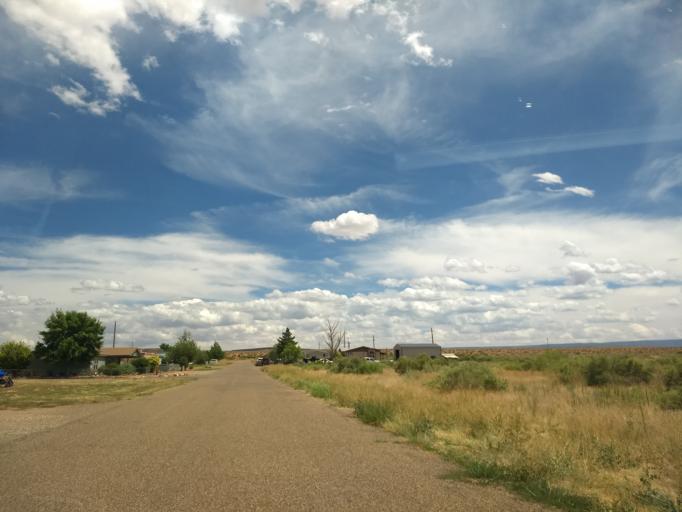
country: US
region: Arizona
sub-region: Coconino County
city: Fredonia
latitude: 36.9595
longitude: -112.5254
